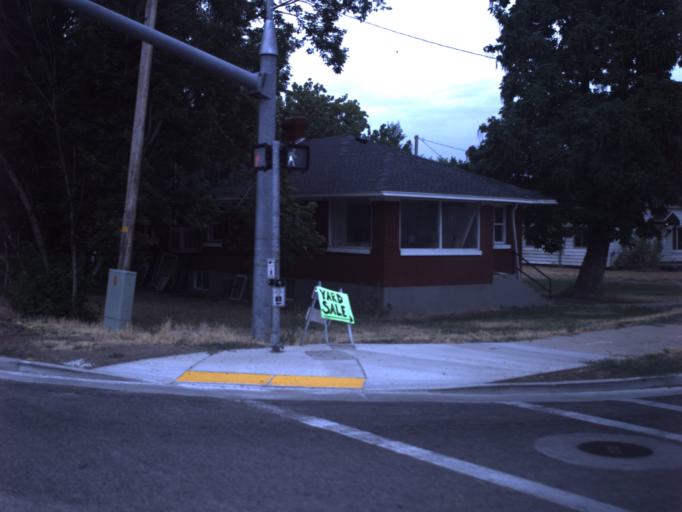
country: US
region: Utah
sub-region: Weber County
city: Harrisville
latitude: 41.2593
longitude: -111.9780
